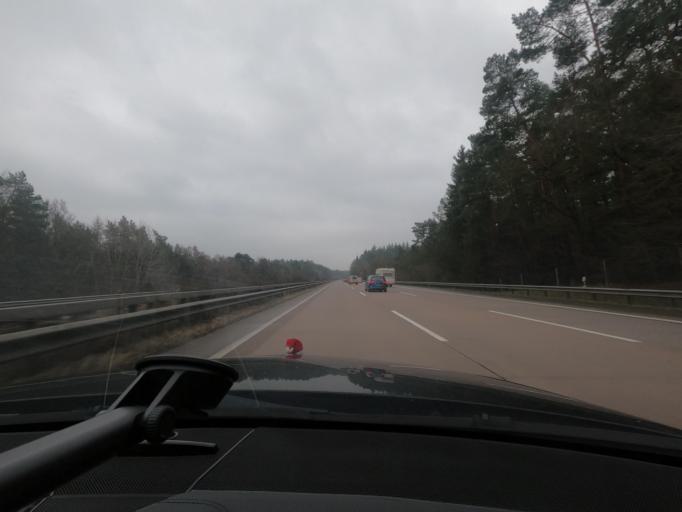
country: DE
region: Lower Saxony
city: Toppenstedt
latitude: 53.2669
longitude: 10.0859
